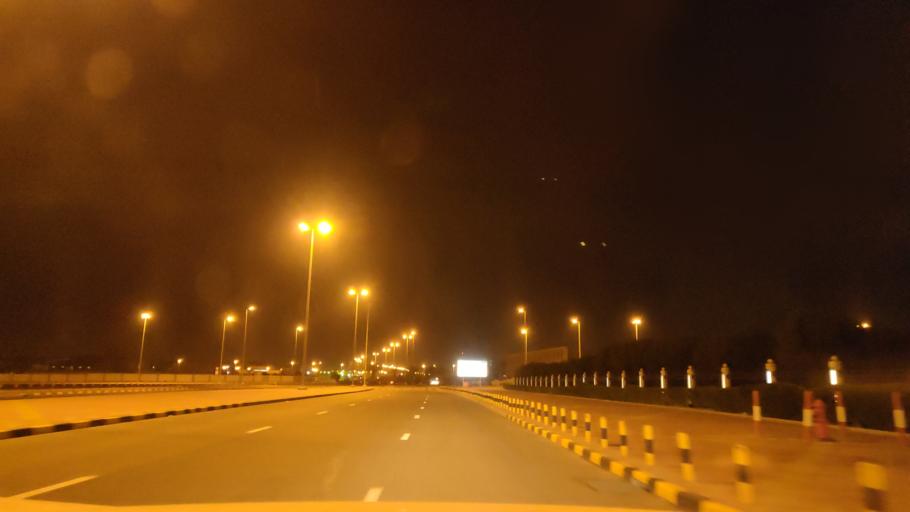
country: KW
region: Al Asimah
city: Ar Rabiyah
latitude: 29.2730
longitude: 47.9160
